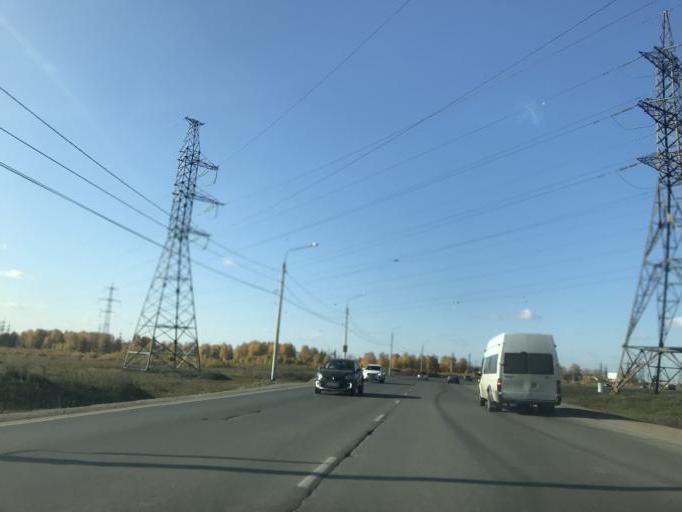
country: RU
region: Chelyabinsk
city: Roshchino
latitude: 55.2250
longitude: 61.2904
